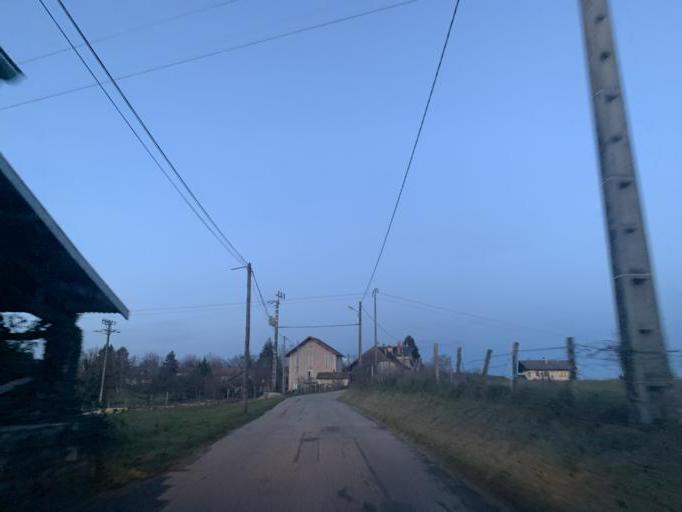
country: FR
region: Rhone-Alpes
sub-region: Departement de l'Ain
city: Belley
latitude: 45.7681
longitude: 5.6973
